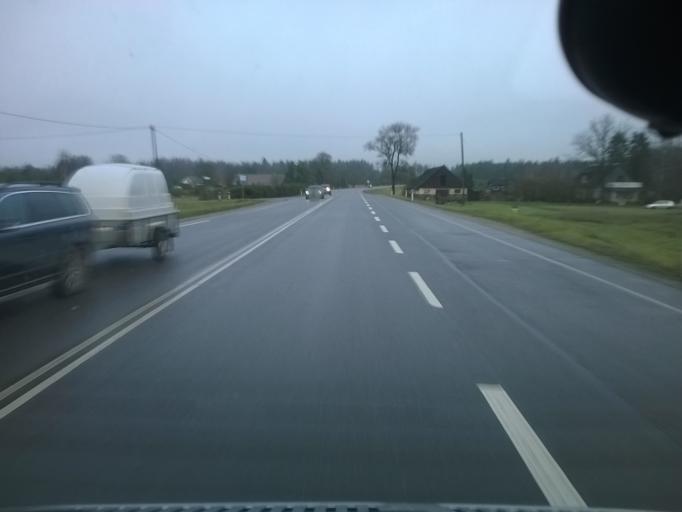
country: EE
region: Harju
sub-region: Saku vald
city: Saku
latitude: 59.3077
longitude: 24.7441
